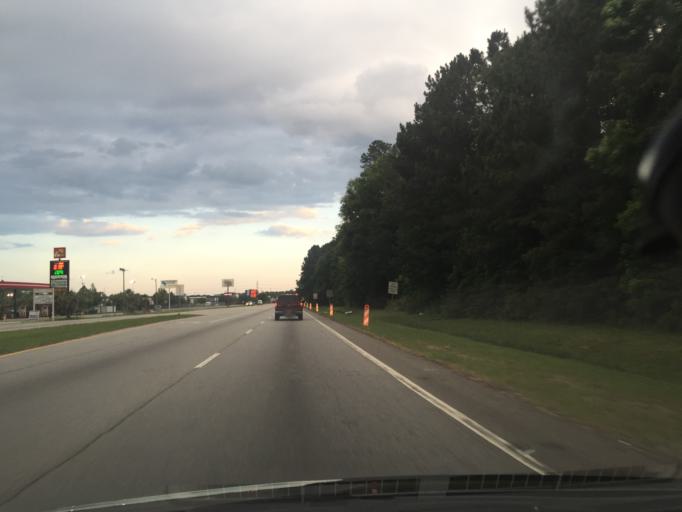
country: US
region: Georgia
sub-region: Chatham County
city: Pooler
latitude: 32.1095
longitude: -81.2322
